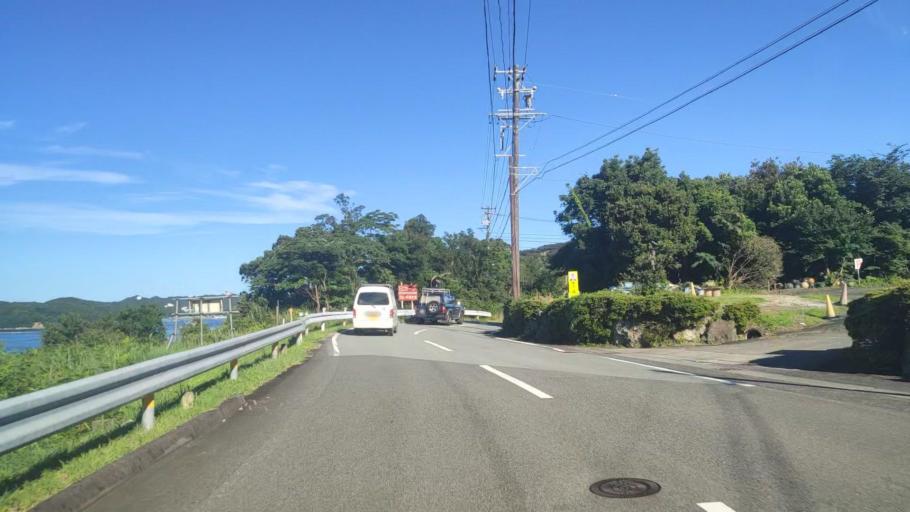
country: JP
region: Mie
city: Toba
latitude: 34.4519
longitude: 136.8751
